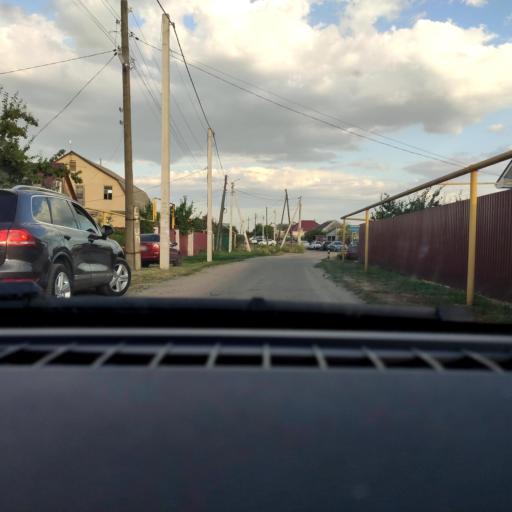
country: RU
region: Voronezj
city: Novaya Usman'
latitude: 51.6710
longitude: 39.3511
